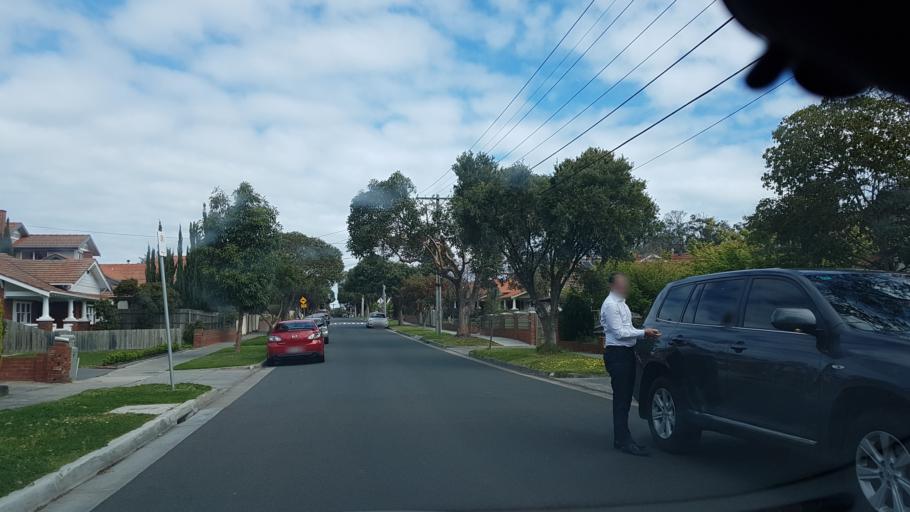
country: AU
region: Victoria
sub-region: Glen Eira
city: Bentleigh
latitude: -37.9192
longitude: 145.0372
